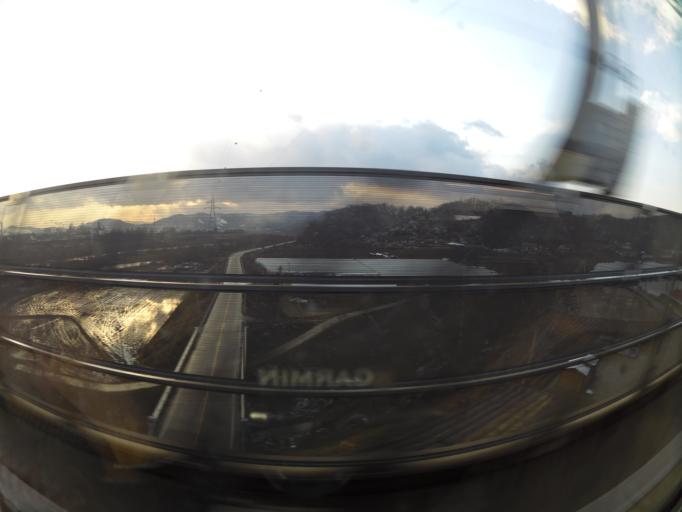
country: KR
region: Daejeon
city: Sintansin
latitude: 36.4568
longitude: 127.4158
